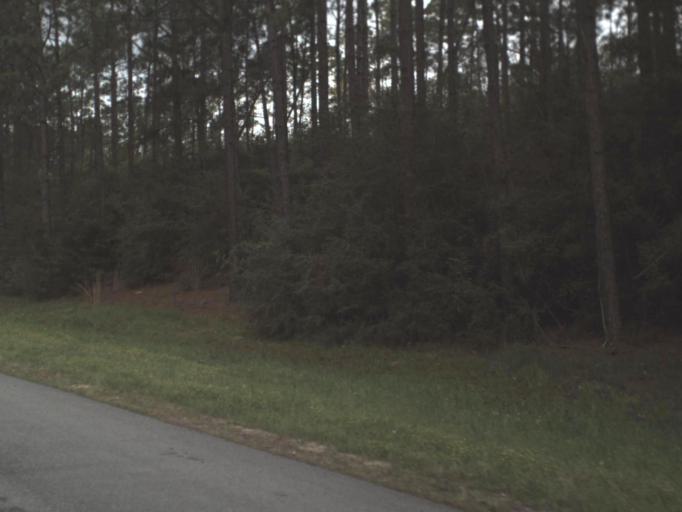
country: US
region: Florida
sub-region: Okaloosa County
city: Crestview
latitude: 30.7215
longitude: -86.5971
